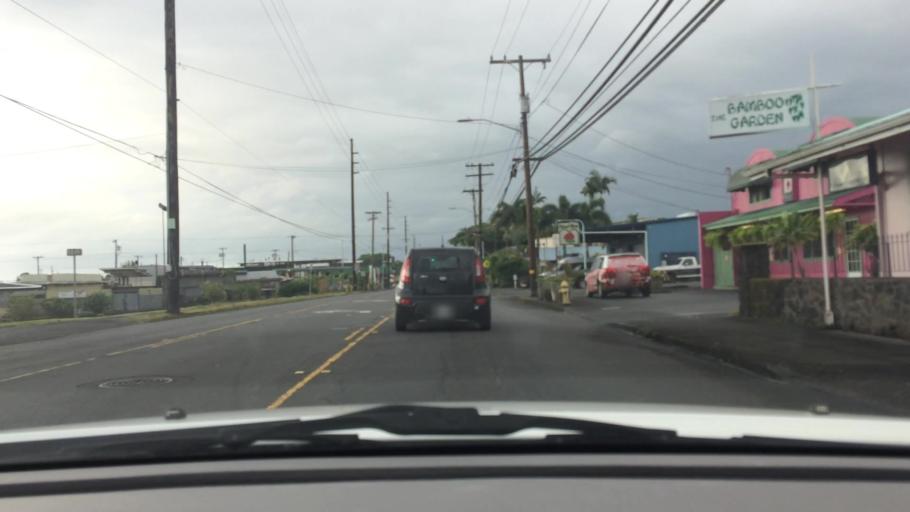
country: US
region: Hawaii
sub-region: Hawaii County
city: Hilo
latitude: 19.7175
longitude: -155.0843
